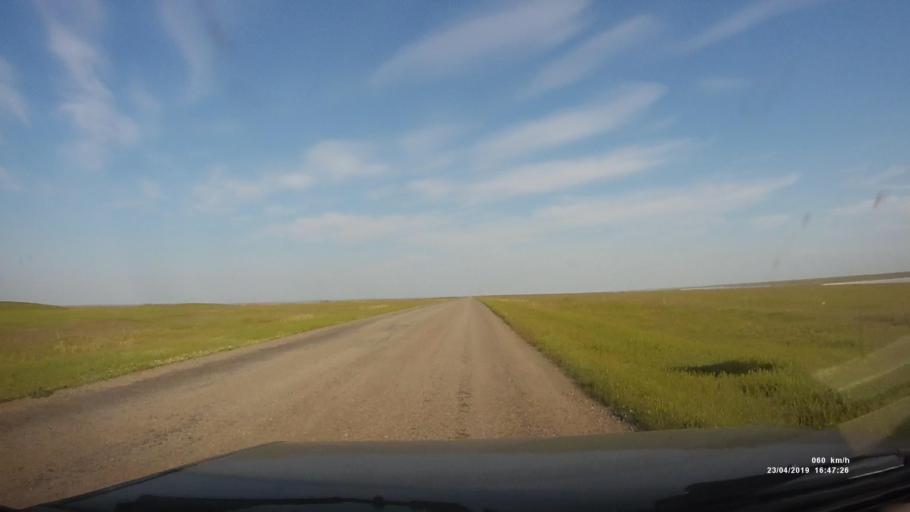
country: RU
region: Kalmykiya
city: Priyutnoye
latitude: 46.3388
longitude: 43.2481
